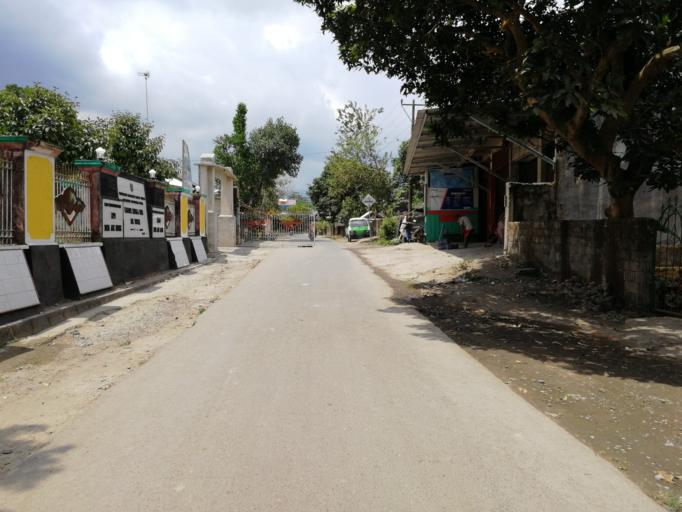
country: ID
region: West Nusa Tenggara
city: Pediti
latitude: -8.5613
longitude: 116.3322
